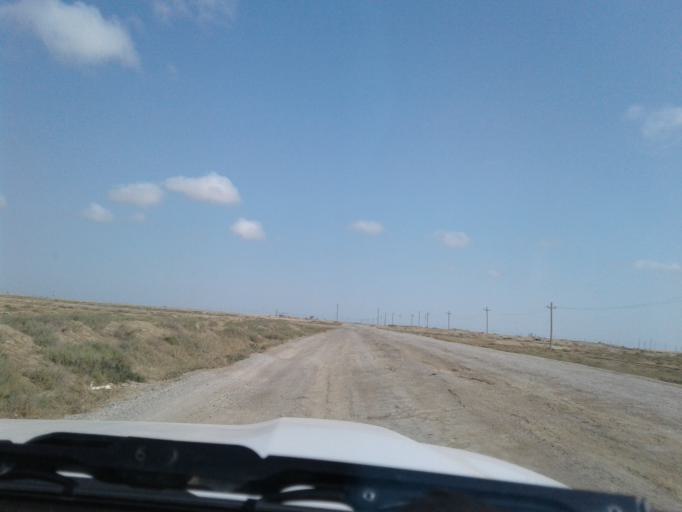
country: IR
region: Golestan
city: Gomishan
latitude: 37.7101
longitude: 53.9407
